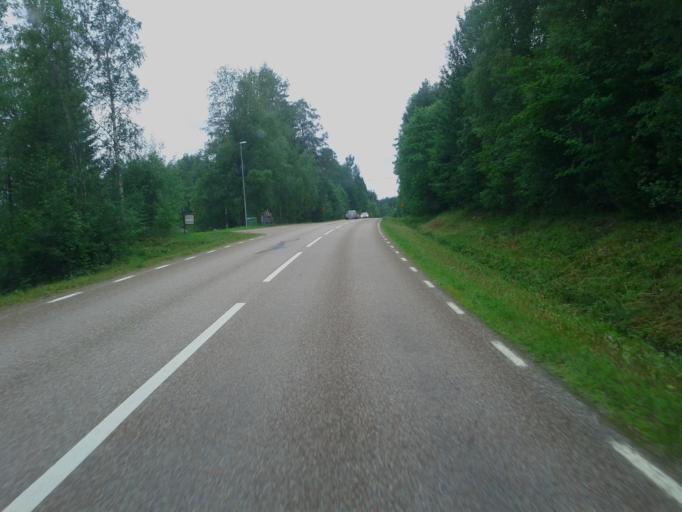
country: SE
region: Dalarna
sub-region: Borlange Kommun
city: Borlaenge
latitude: 60.3330
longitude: 15.3966
